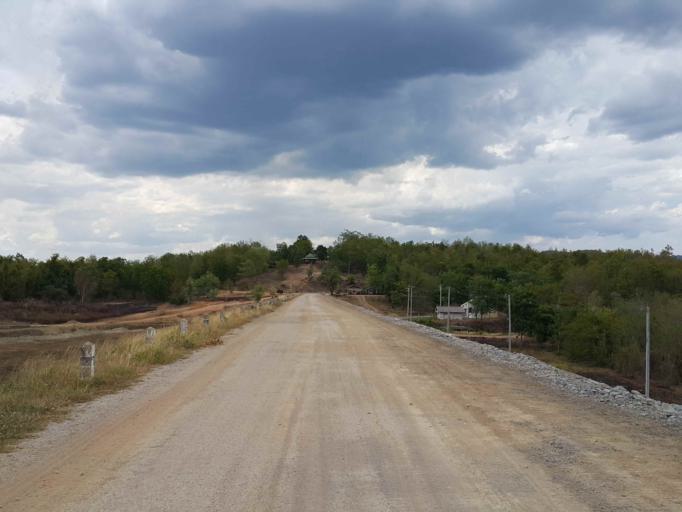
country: TH
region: Sukhothai
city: Thung Saliam
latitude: 17.3251
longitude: 99.4223
